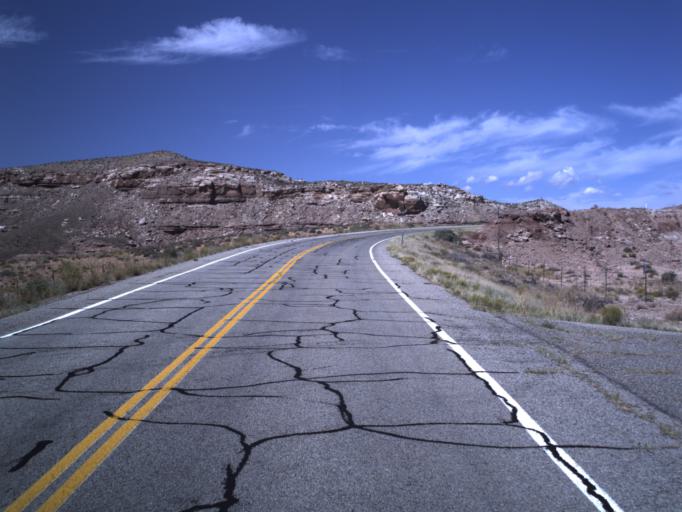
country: US
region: Utah
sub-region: San Juan County
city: Blanding
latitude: 37.2828
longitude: -109.3827
